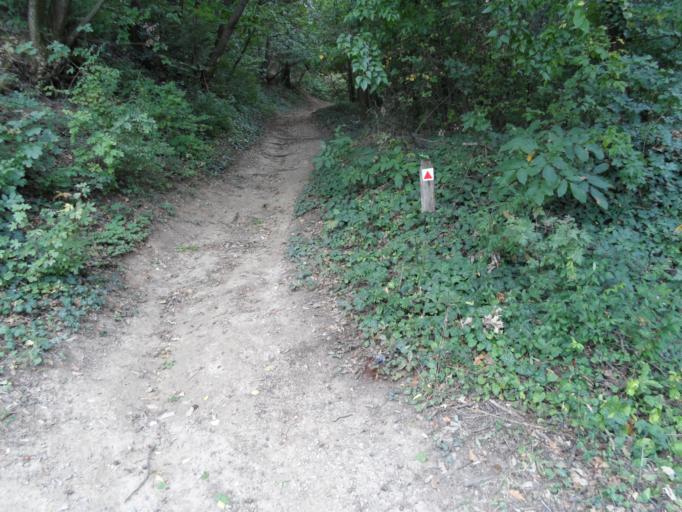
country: HU
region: Somogy
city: Fonyod
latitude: 46.7462
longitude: 17.5525
